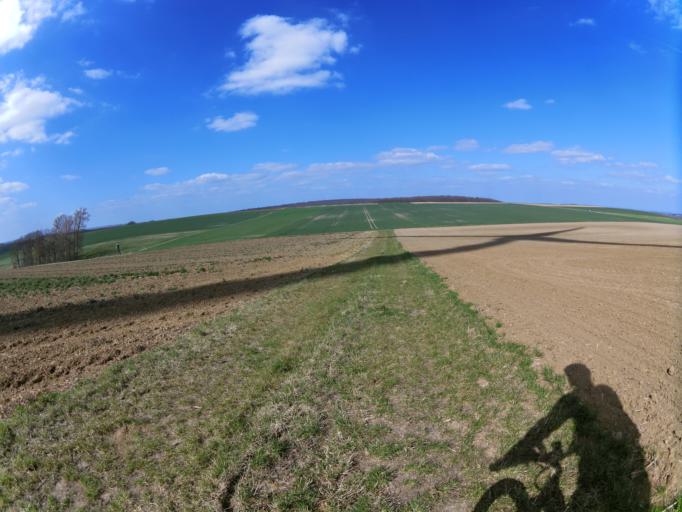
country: DE
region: Bavaria
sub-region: Regierungsbezirk Unterfranken
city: Dettelbach
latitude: 49.8321
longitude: 10.1632
